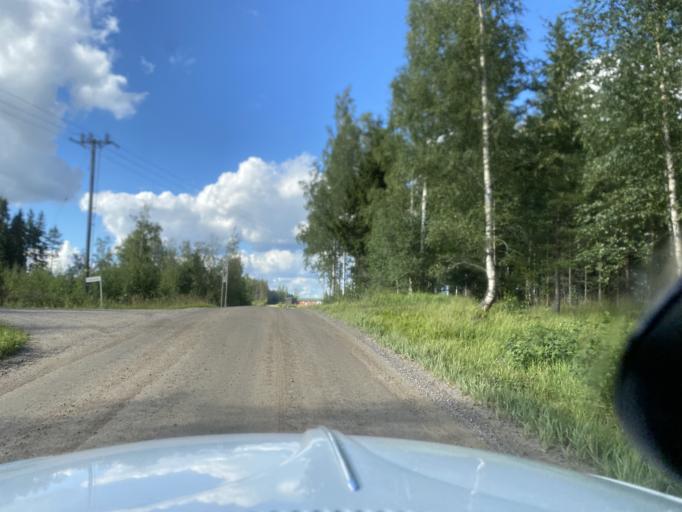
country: FI
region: Pirkanmaa
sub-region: Lounais-Pirkanmaa
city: Punkalaidun
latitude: 61.1113
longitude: 23.2748
